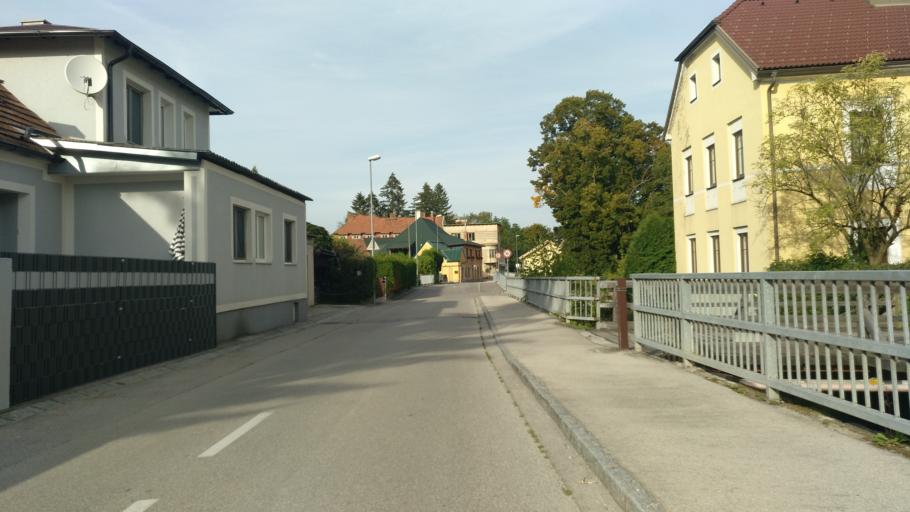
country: AT
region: Lower Austria
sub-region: Politischer Bezirk Sankt Polten
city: Wilhelmsburg
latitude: 48.0973
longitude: 15.5967
